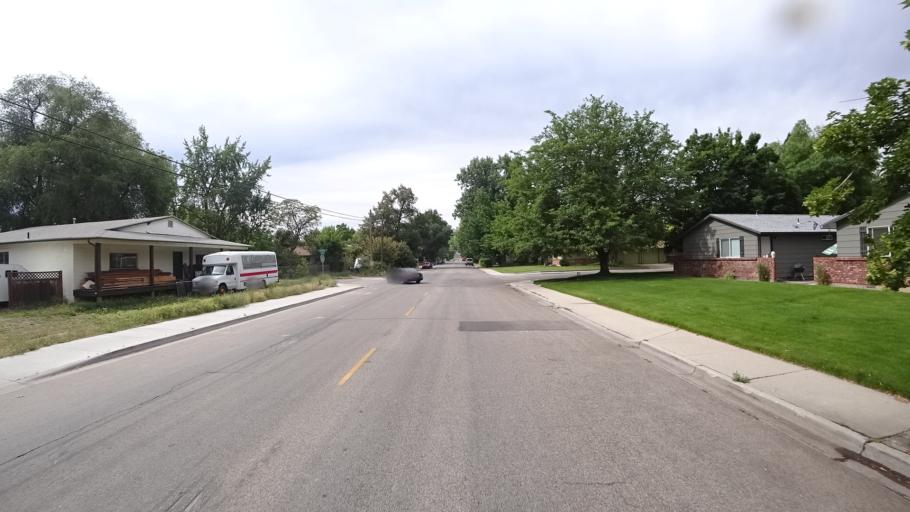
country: US
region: Idaho
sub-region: Ada County
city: Boise
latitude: 43.5855
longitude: -116.2237
